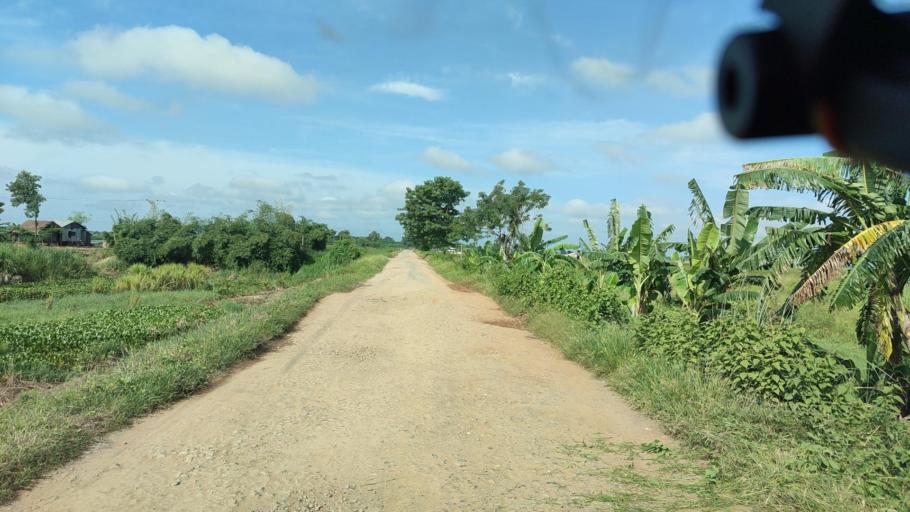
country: MM
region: Bago
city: Letpandan
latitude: 17.7638
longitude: 95.6847
